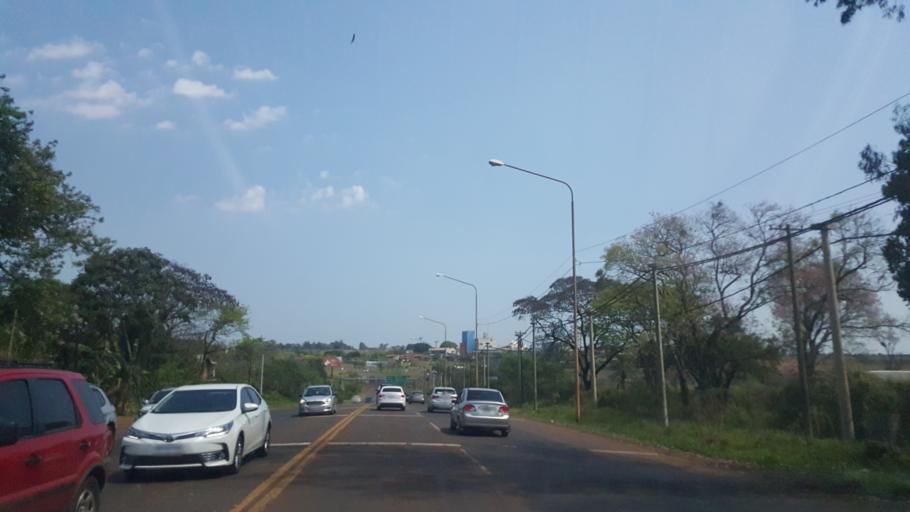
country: AR
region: Misiones
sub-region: Departamento de Capital
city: Posadas
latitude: -27.3986
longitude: -55.9531
